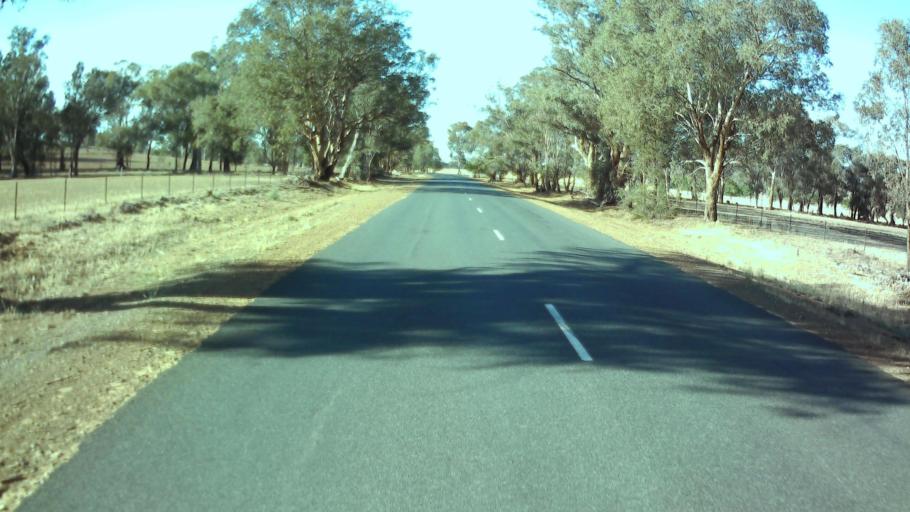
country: AU
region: New South Wales
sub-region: Weddin
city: Grenfell
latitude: -33.9408
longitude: 148.1364
